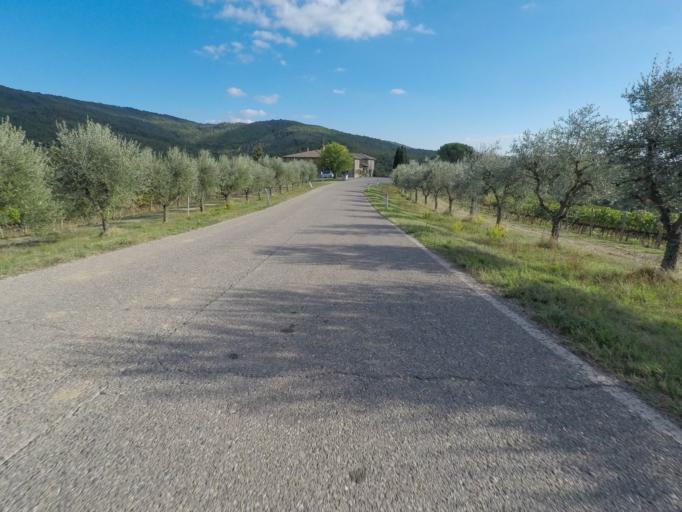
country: IT
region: Tuscany
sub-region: Provincia di Siena
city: Radda in Chianti
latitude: 43.5145
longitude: 11.4068
